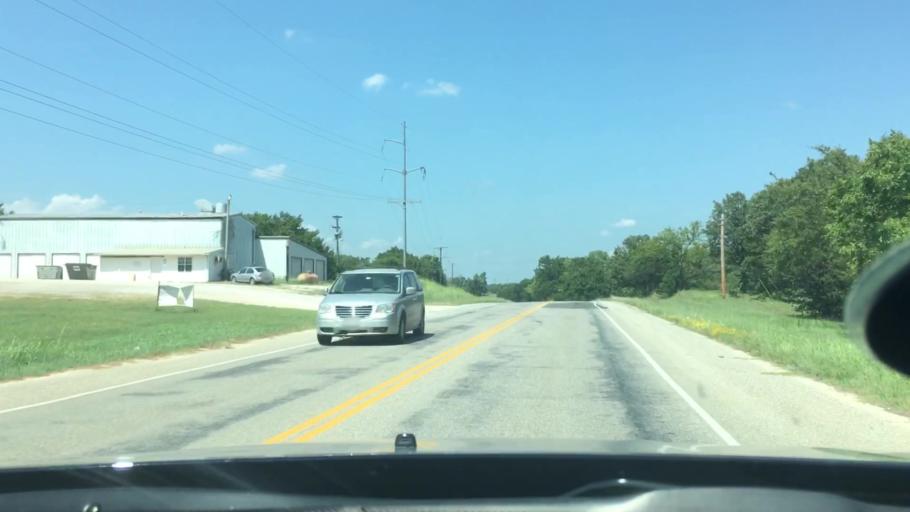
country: US
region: Oklahoma
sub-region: Pontotoc County
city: Byng
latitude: 34.8298
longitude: -96.6786
